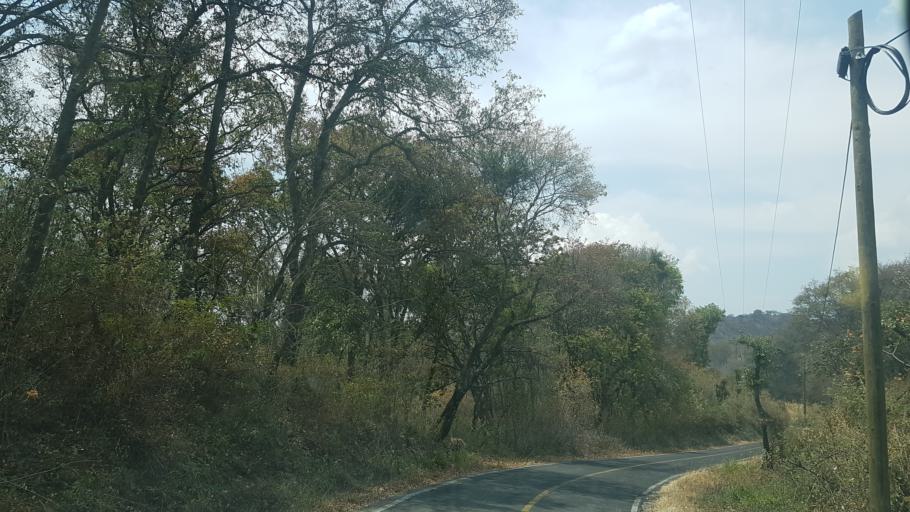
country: MX
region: Puebla
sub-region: Tochimilco
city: La Magdalena Yancuitlalpan
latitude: 18.8838
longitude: -98.5910
